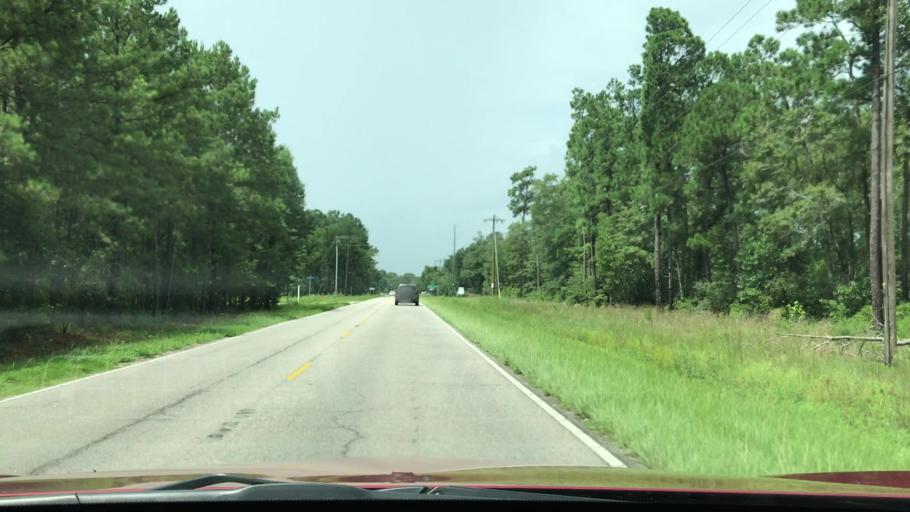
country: US
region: South Carolina
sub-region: Horry County
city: Red Hill
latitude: 33.8939
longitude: -78.9429
